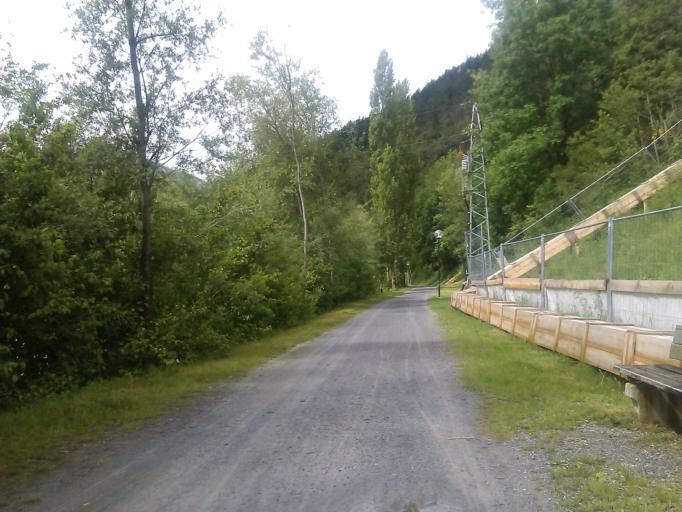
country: AT
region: Tyrol
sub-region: Politischer Bezirk Landeck
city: Zams
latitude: 47.1565
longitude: 10.5734
